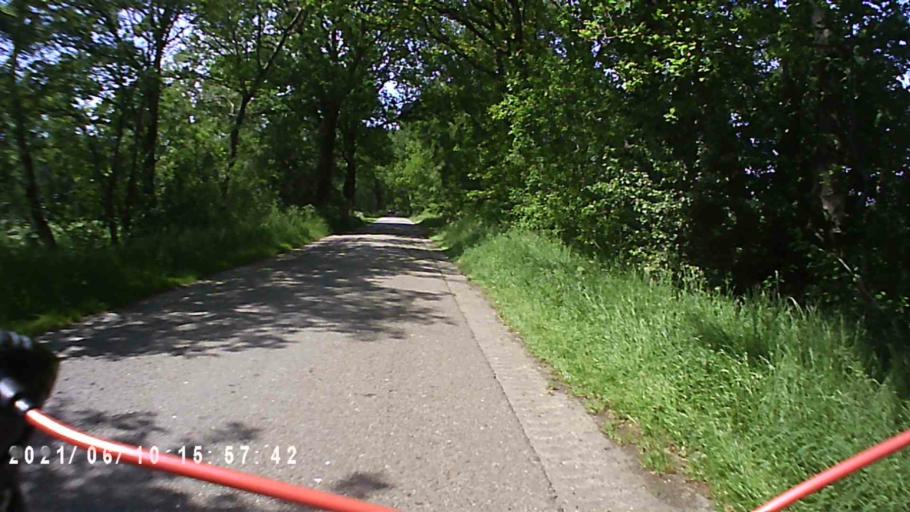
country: NL
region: Friesland
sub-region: Gemeente Achtkarspelen
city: Drogeham
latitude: 53.1898
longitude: 6.0938
